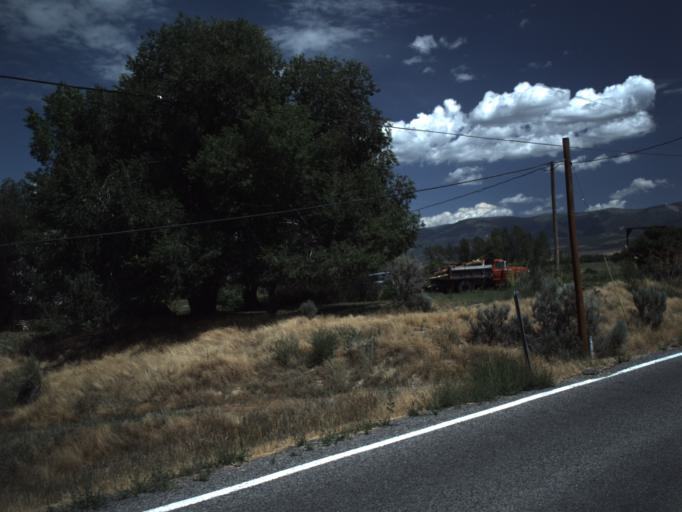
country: US
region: Utah
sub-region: Sanpete County
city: Mount Pleasant
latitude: 39.4818
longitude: -111.5120
